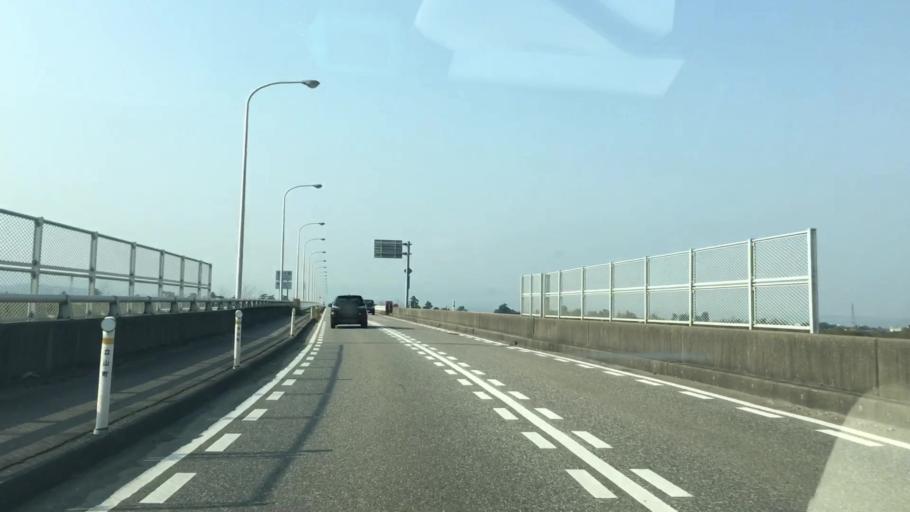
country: JP
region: Toyama
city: Kamiichi
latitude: 36.6268
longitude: 137.3005
